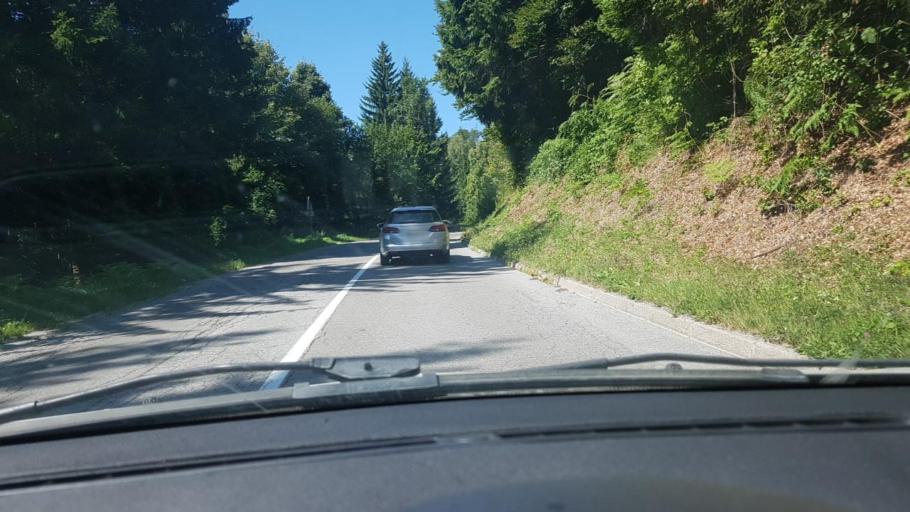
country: HR
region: Primorsko-Goranska
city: Vrbovsko
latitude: 45.3770
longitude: 14.9714
